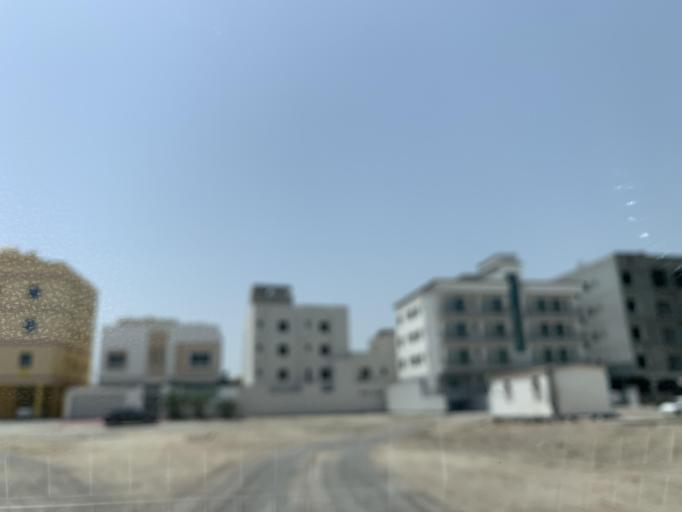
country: BH
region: Northern
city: Madinat `Isa
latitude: 26.1898
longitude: 50.5493
